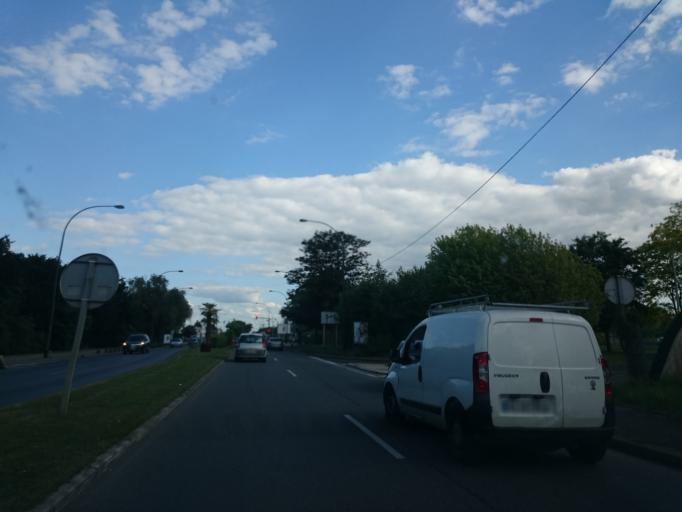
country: FR
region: Ile-de-France
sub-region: Departement de l'Essonne
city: Evry
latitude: 48.6151
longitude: 2.4572
